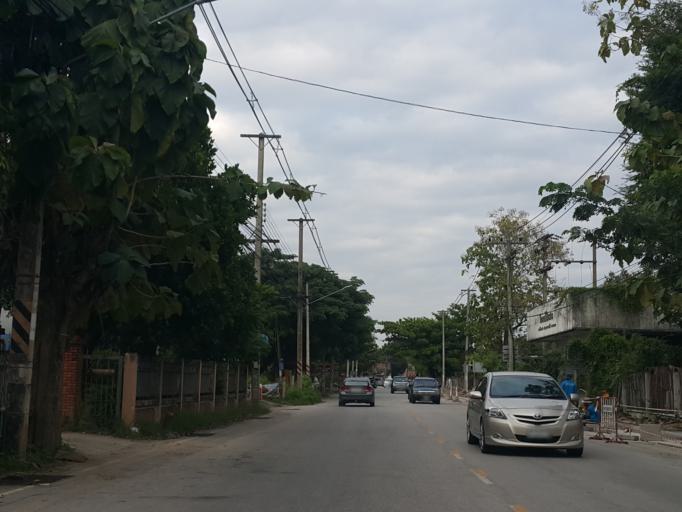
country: TH
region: Lampang
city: Lampang
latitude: 18.2997
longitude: 99.5051
